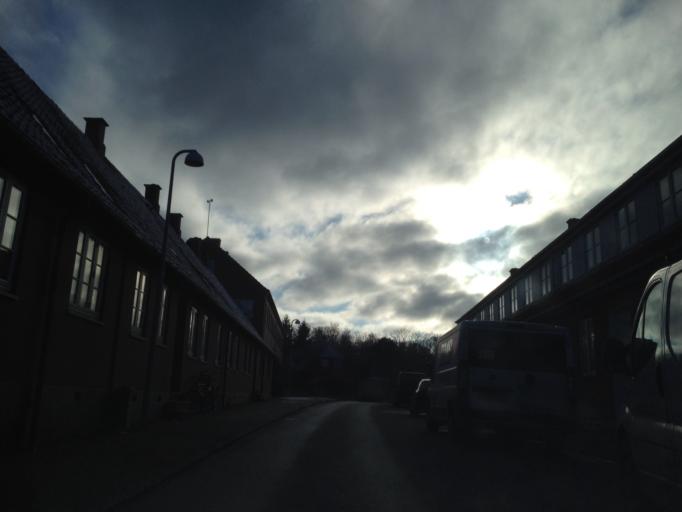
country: DK
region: Capital Region
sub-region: Helsingor Kommune
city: Hellebaek
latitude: 56.0704
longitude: 12.5563
